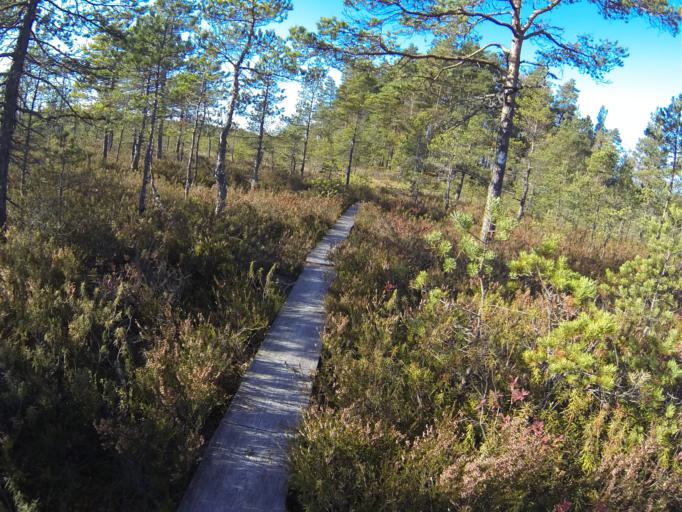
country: FI
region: Varsinais-Suomi
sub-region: Salo
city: Saerkisalo
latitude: 60.2178
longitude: 22.9602
